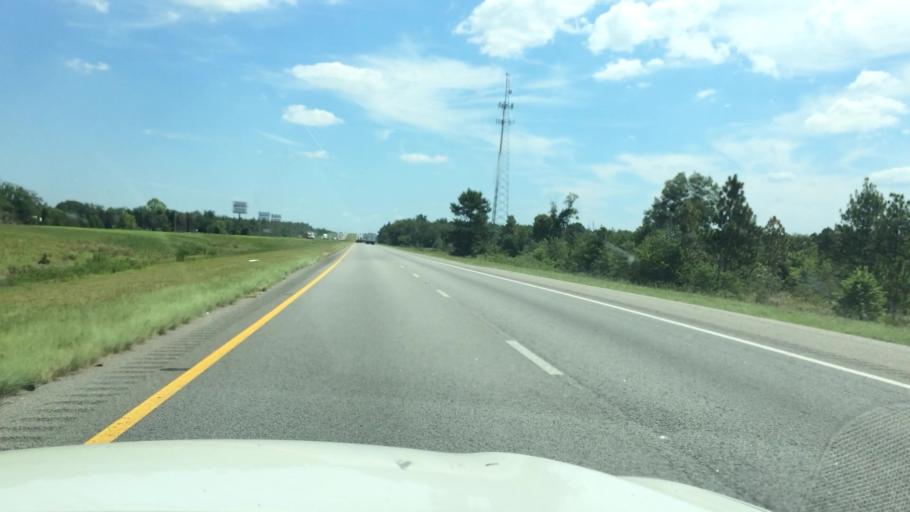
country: US
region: South Carolina
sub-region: Lexington County
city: Batesburg
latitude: 33.7107
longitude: -81.5827
